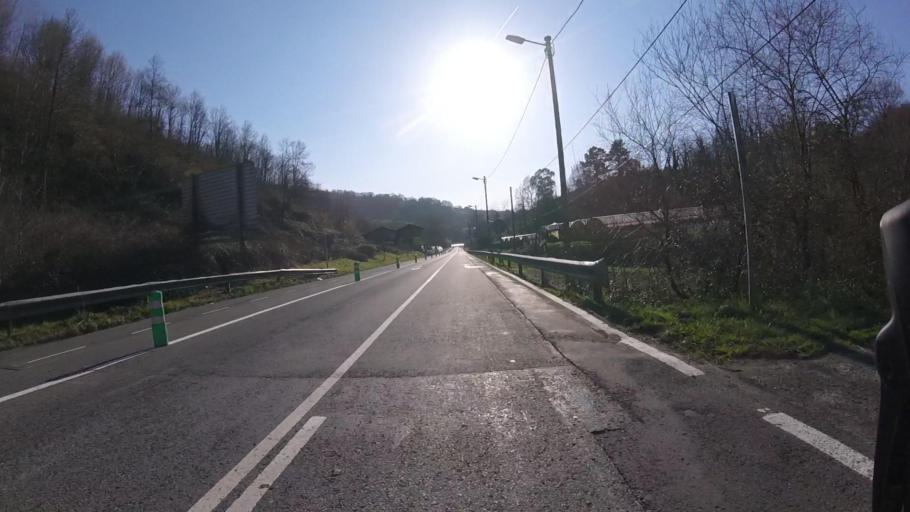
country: ES
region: Basque Country
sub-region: Provincia de Guipuzcoa
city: Astigarraga
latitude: 43.2860
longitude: -1.9361
